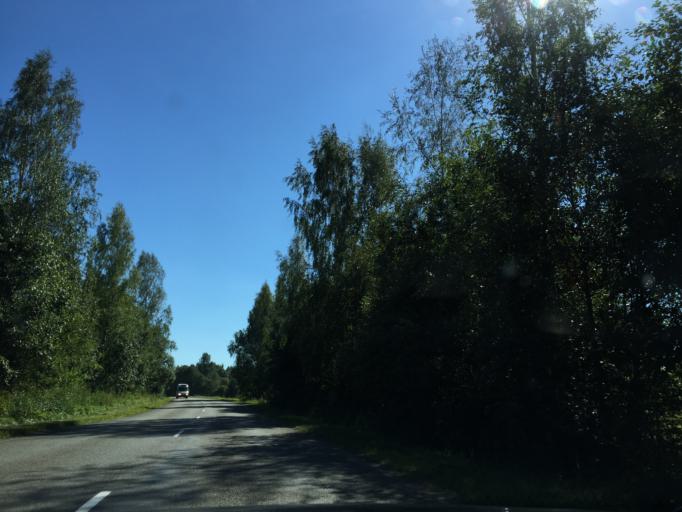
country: LV
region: Akniste
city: Akniste
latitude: 56.1220
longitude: 25.8309
